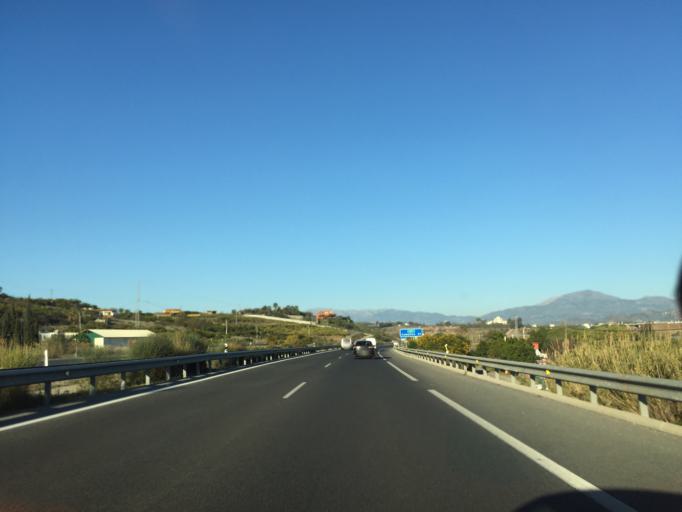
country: ES
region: Andalusia
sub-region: Provincia de Malaga
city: Cartama
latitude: 36.7146
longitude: -4.6549
